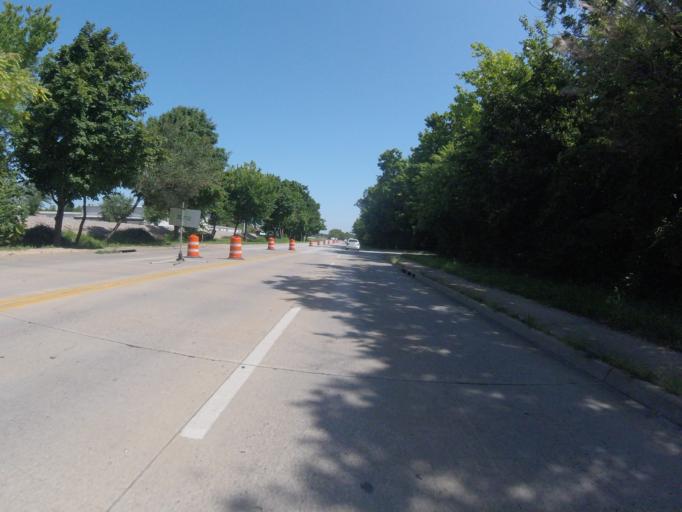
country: US
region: Arkansas
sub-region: Washington County
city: Fayetteville
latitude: 36.0902
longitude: -94.1619
